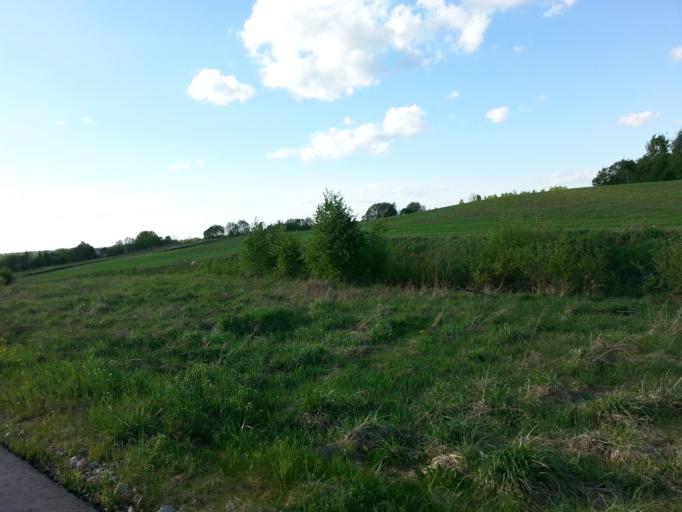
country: BY
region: Minsk
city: Narach
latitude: 54.9394
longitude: 26.6988
